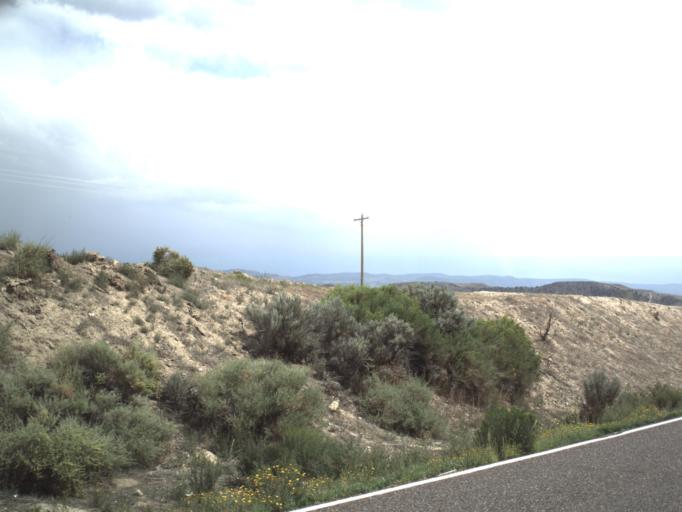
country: US
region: Utah
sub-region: Piute County
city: Junction
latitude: 38.1449
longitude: -111.9984
